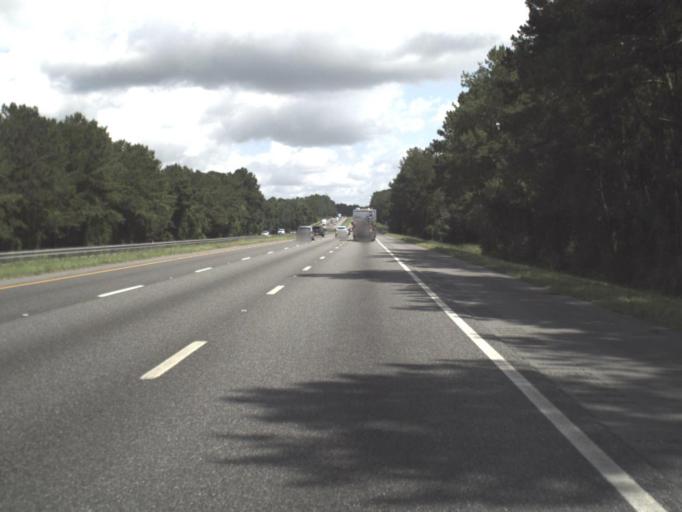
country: US
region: Florida
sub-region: Alachua County
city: High Springs
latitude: 29.9287
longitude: -82.5595
